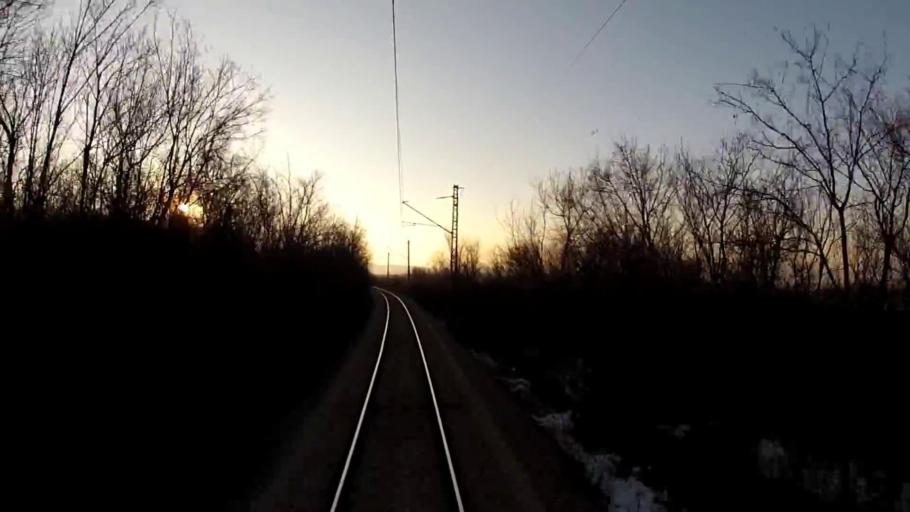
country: BG
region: Sofiya
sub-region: Obshtina Dragoman
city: Dragoman
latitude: 42.8981
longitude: 22.9603
